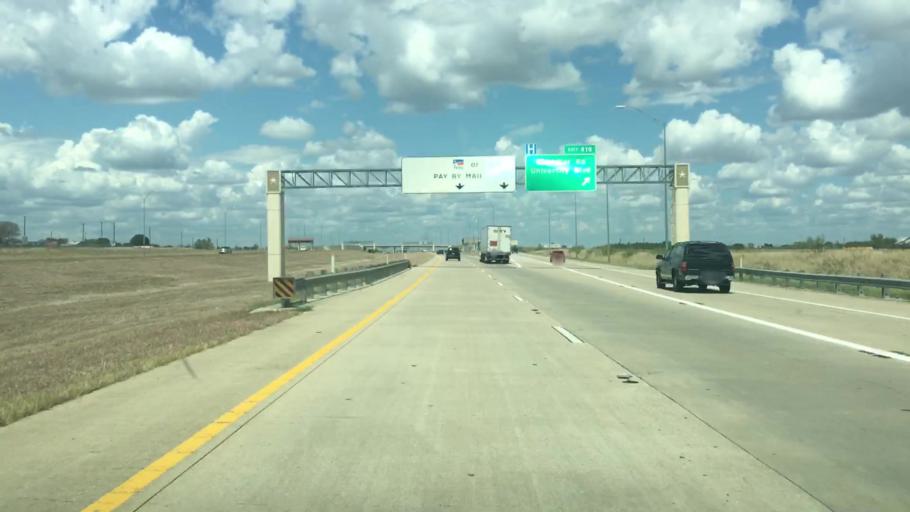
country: US
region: Texas
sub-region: Williamson County
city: Hutto
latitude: 30.5806
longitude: -97.5866
